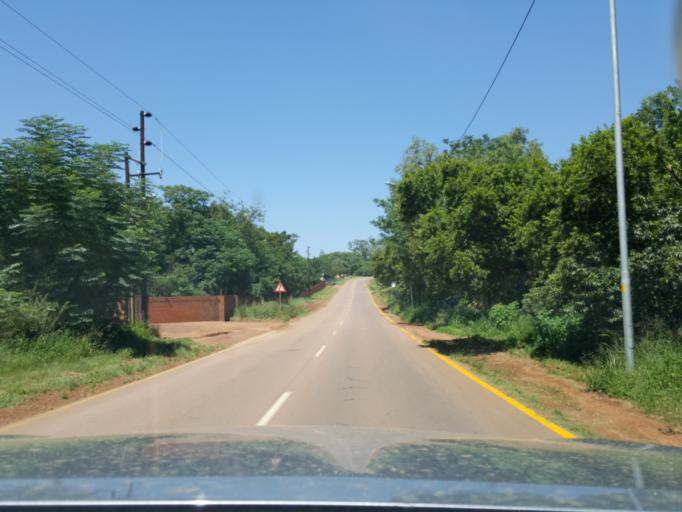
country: ZA
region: Gauteng
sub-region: City of Tshwane Metropolitan Municipality
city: Pretoria
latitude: -25.6632
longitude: 28.3099
